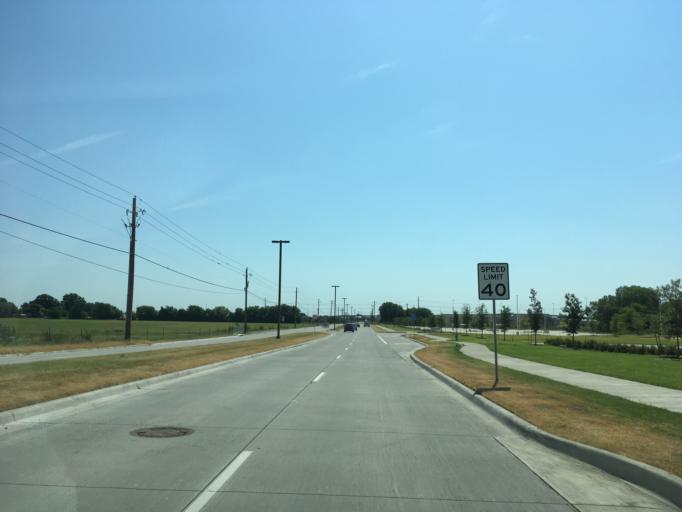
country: US
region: Texas
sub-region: Collin County
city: Fairview
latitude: 33.1590
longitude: -96.6605
